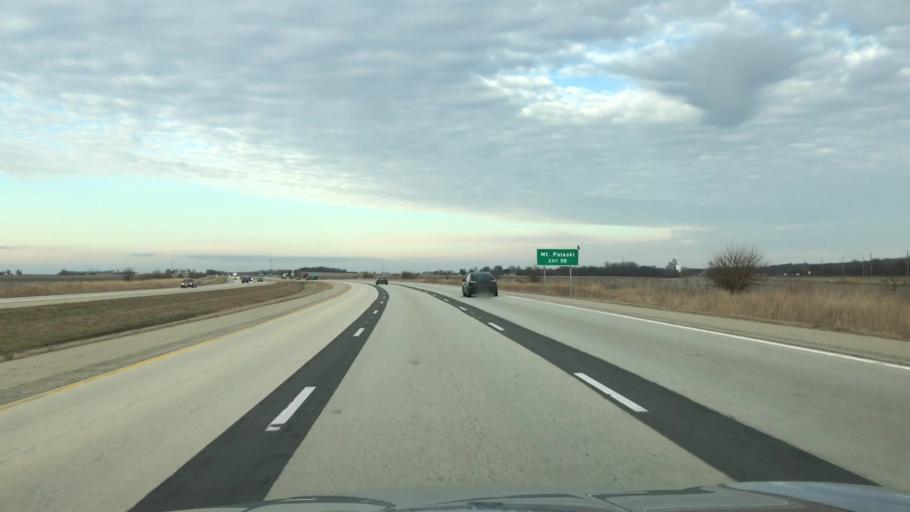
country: US
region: Illinois
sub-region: Sangamon County
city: Williamsville
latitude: 40.0042
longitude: -89.5019
